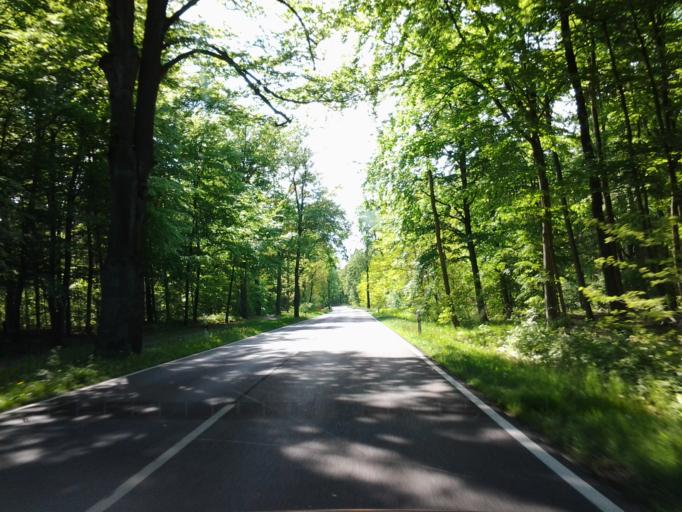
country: DE
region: Brandenburg
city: Oranienburg
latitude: 52.7643
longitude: 13.2975
